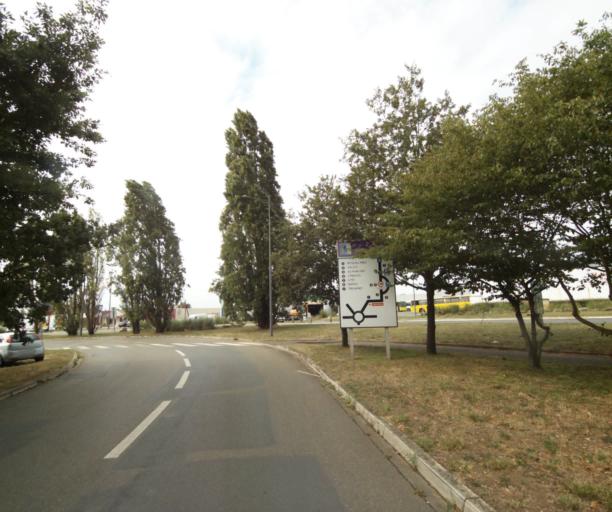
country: FR
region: Pays de la Loire
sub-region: Departement de la Sarthe
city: Solesmes
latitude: 47.8276
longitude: -0.3076
